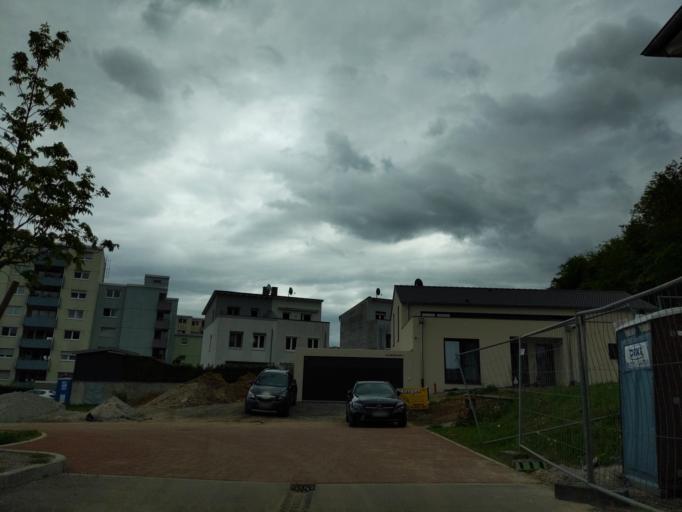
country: DE
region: Baden-Wuerttemberg
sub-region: Karlsruhe Region
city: Mauer
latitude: 49.3359
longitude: 8.7859
